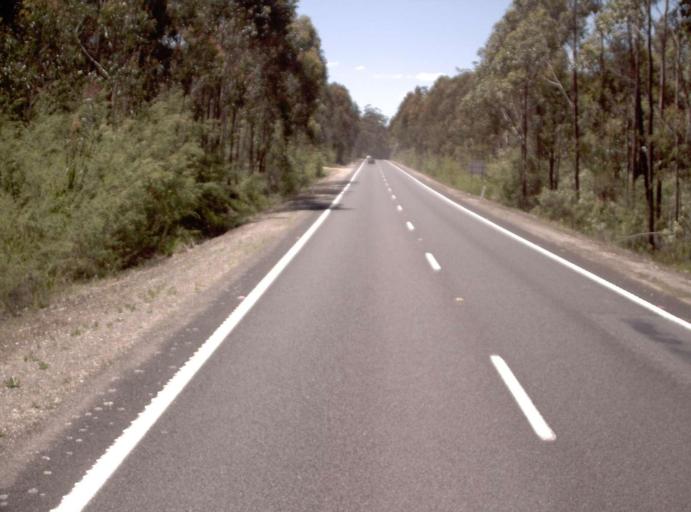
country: AU
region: Victoria
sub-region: East Gippsland
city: Lakes Entrance
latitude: -37.6956
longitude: 148.6123
